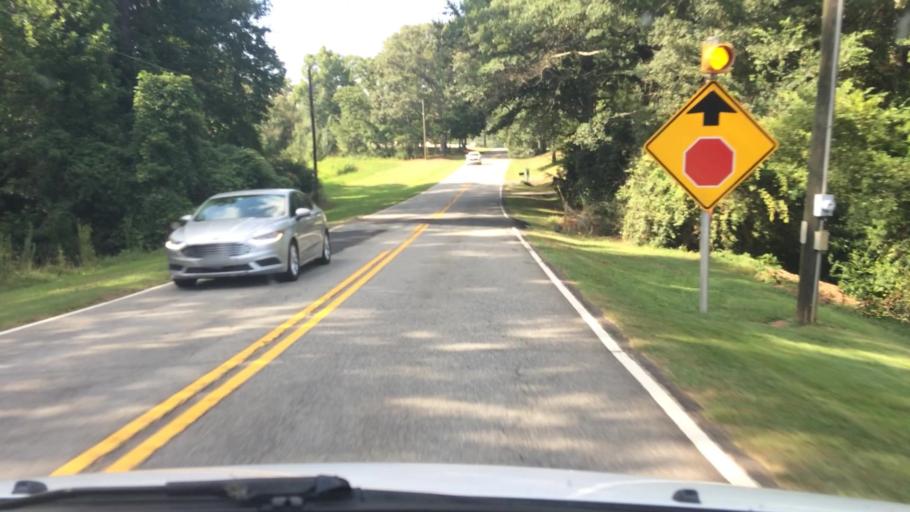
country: US
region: South Carolina
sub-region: Anderson County
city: Anderson
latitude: 34.5593
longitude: -82.6109
